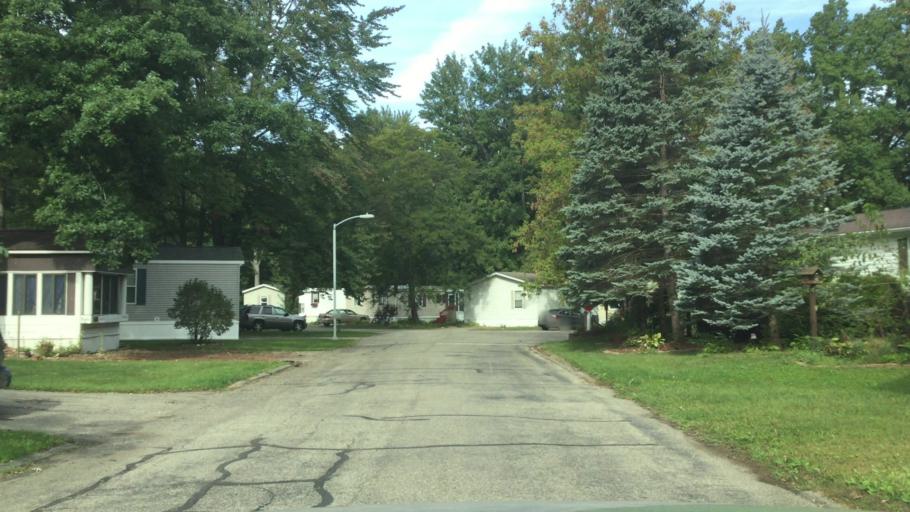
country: US
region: Michigan
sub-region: Oakland County
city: Holly
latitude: 42.8130
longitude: -83.6219
